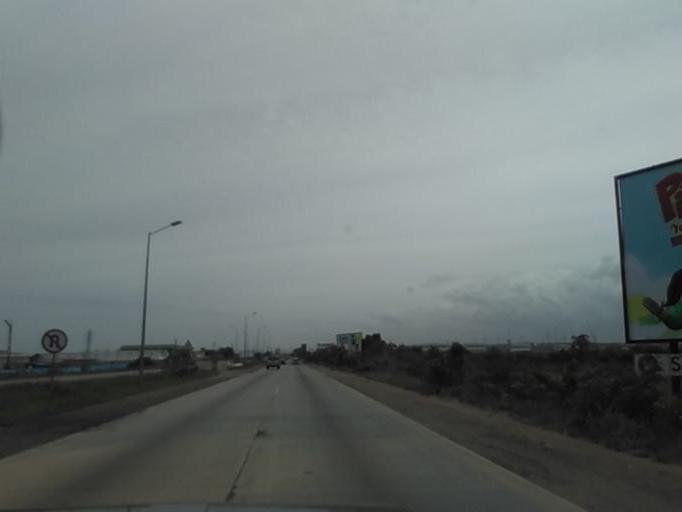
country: GH
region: Greater Accra
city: Tema
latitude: 5.6658
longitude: -0.0632
